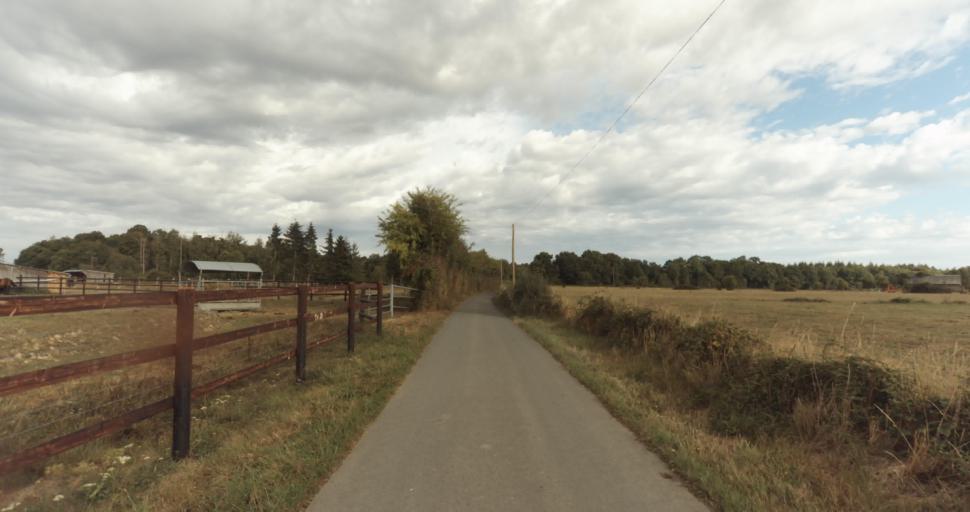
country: FR
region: Lower Normandy
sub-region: Departement de l'Orne
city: Vimoutiers
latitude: 48.9581
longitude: 0.2483
